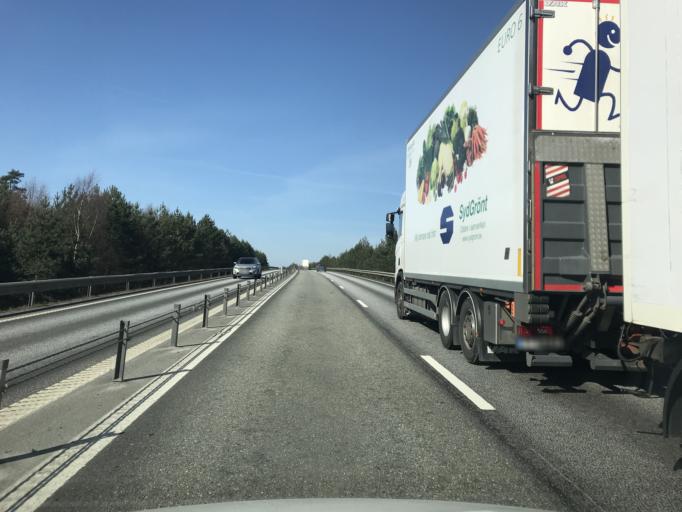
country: SE
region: Skane
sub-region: Hassleholms Kommun
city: Hassleholm
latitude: 56.1826
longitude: 13.7886
